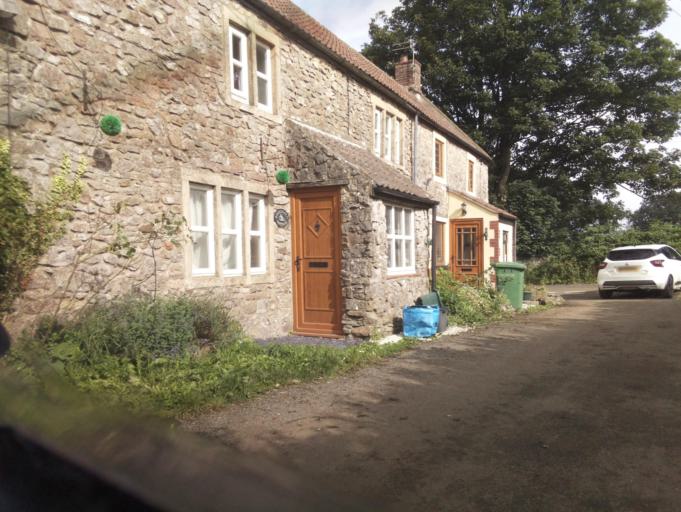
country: GB
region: England
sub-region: Somerset
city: Chilcompton
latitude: 51.2233
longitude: -2.5004
